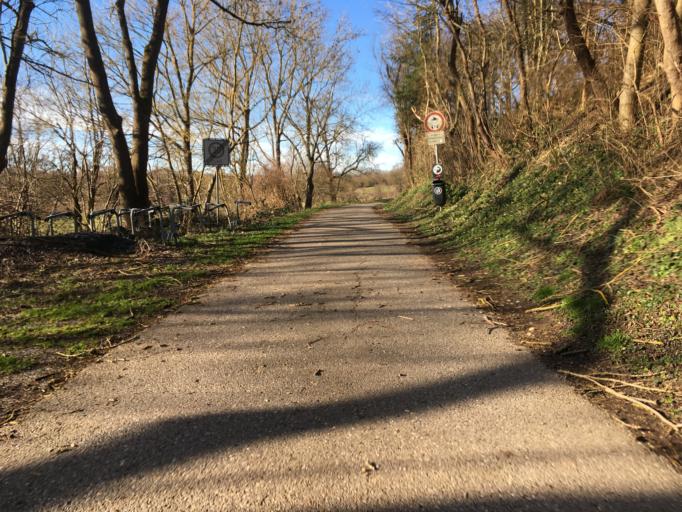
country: DE
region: Baden-Wuerttemberg
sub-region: Regierungsbezirk Stuttgart
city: Eppingen
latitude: 49.1441
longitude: 8.9009
